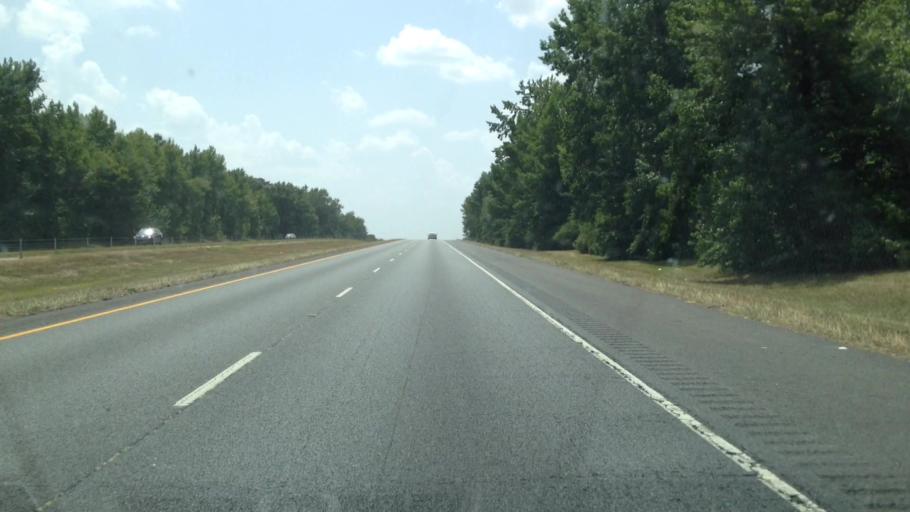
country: US
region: Louisiana
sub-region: Lincoln Parish
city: Grambling
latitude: 32.5441
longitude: -92.7377
